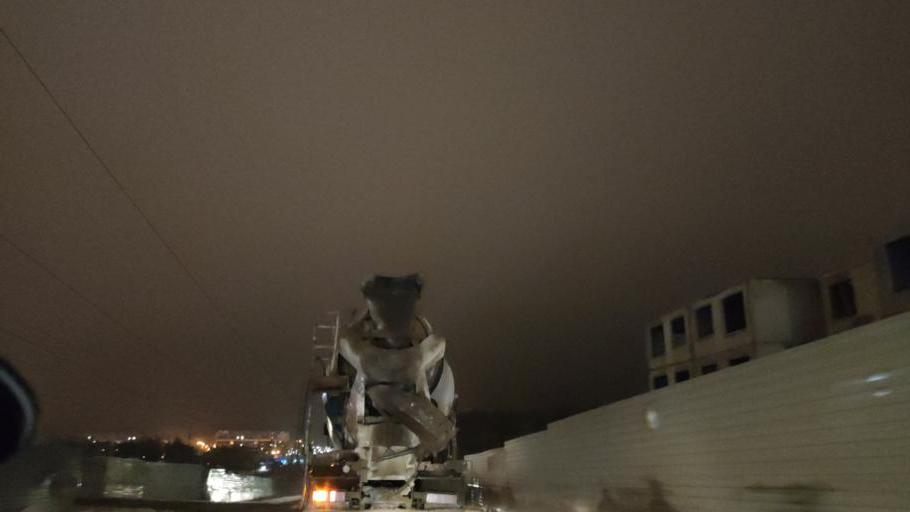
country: RU
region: Moscow
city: Zagor'ye
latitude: 55.5302
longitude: 37.6377
